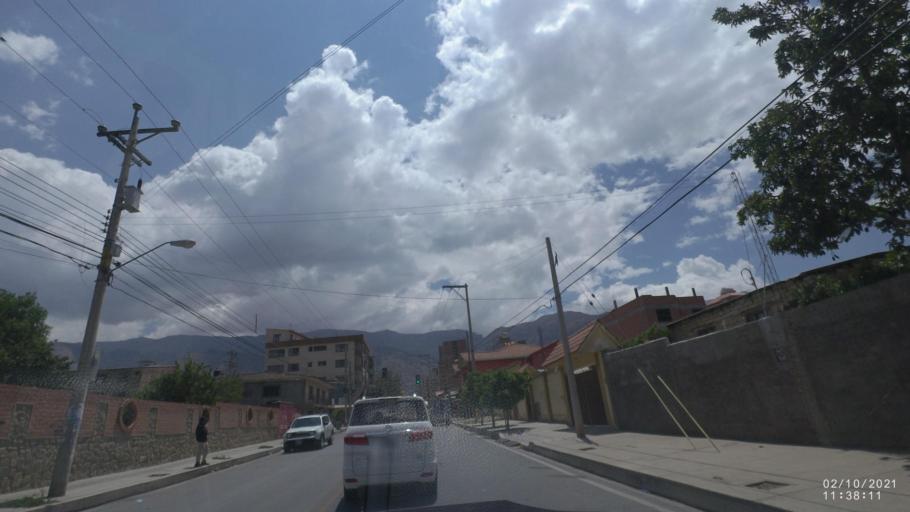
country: BO
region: Cochabamba
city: Cochabamba
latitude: -17.3403
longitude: -66.2219
